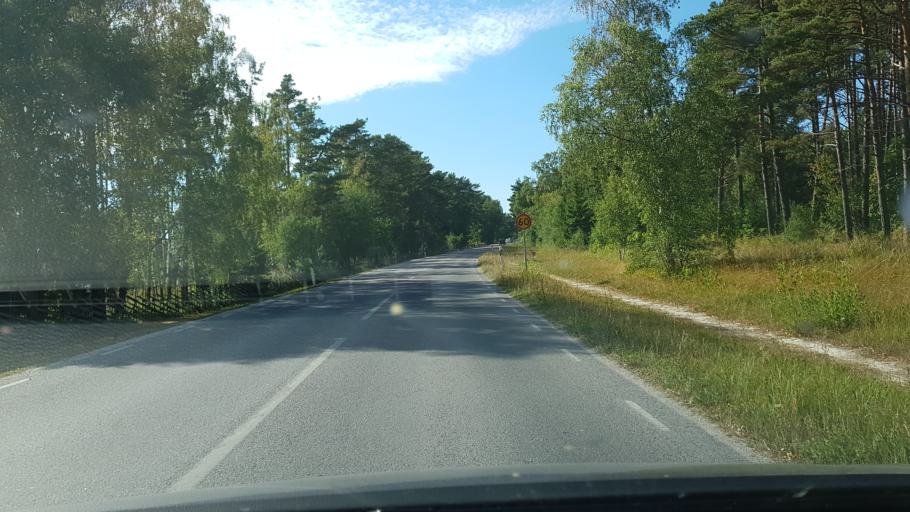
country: SE
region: Gotland
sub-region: Gotland
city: Klintehamn
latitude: 57.4055
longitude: 18.1735
